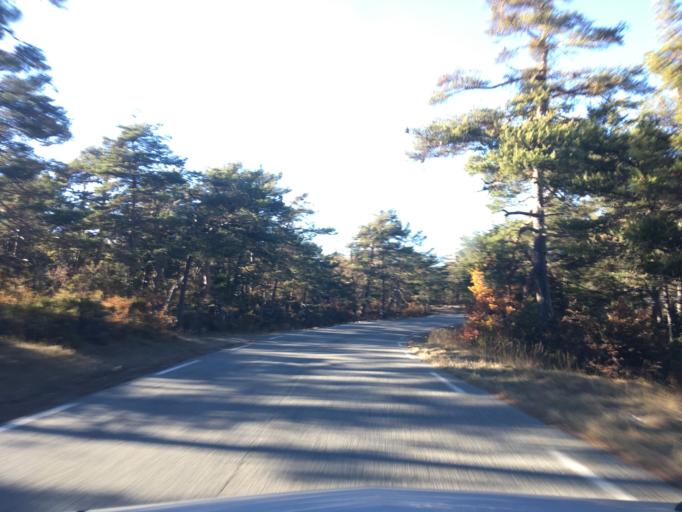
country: FR
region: Provence-Alpes-Cote d'Azur
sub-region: Departement du Var
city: Montferrat
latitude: 43.7401
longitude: 6.4271
